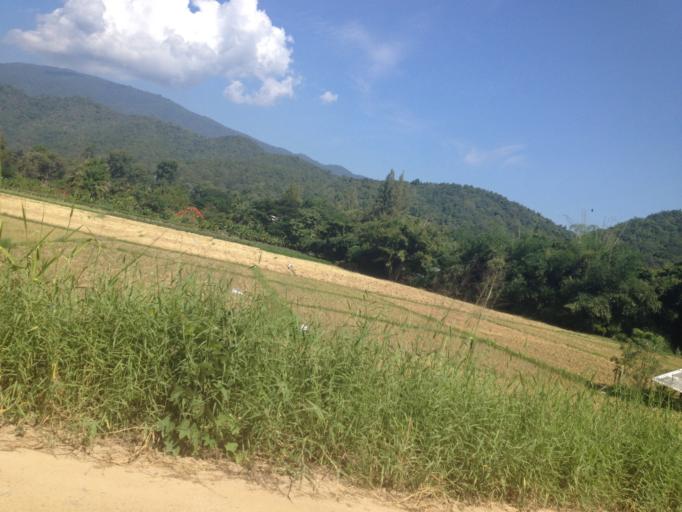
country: TH
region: Chiang Mai
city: Hang Dong
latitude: 18.7447
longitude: 98.8885
